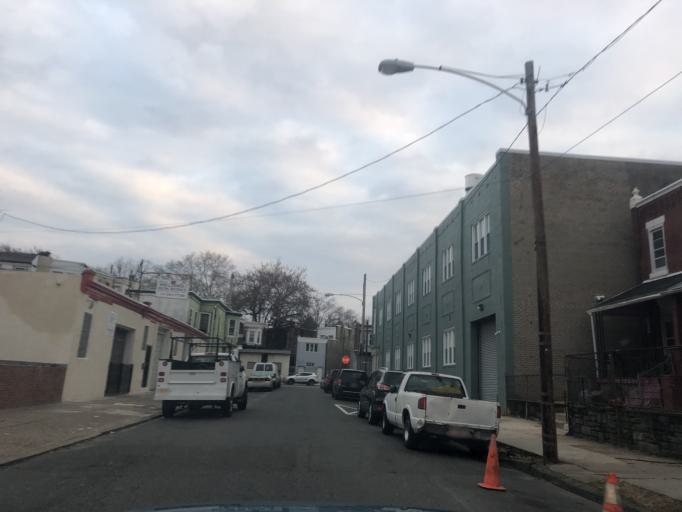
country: US
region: Pennsylvania
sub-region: Delaware County
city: Millbourne
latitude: 39.9693
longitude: -75.2403
